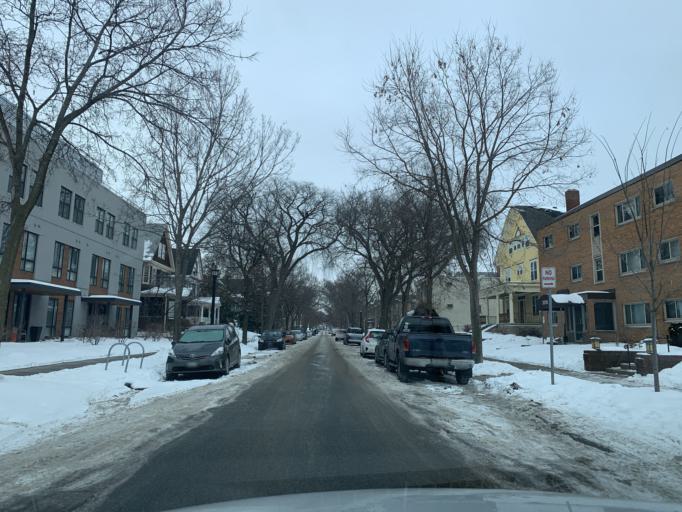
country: US
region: Minnesota
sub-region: Hennepin County
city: Minneapolis
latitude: 44.9592
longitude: -93.2918
